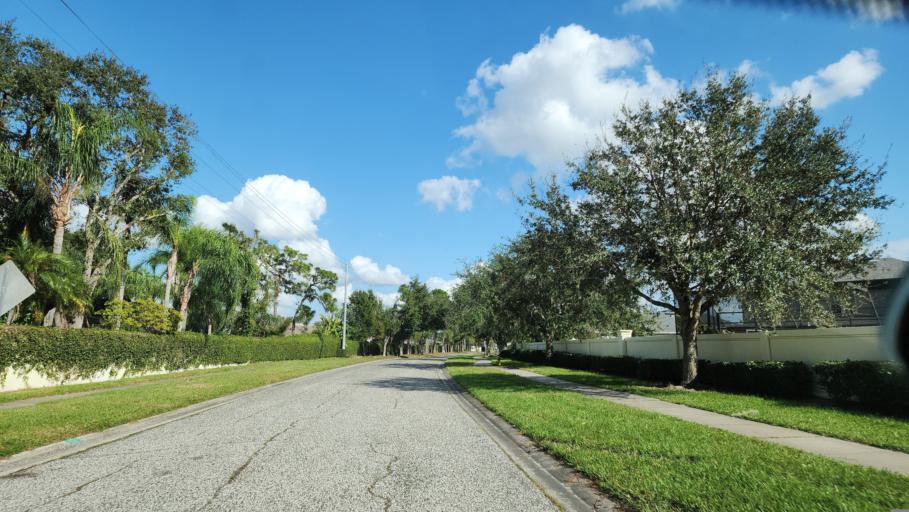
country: US
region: Florida
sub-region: Hillsborough County
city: Riverview
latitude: 27.8037
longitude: -82.3107
